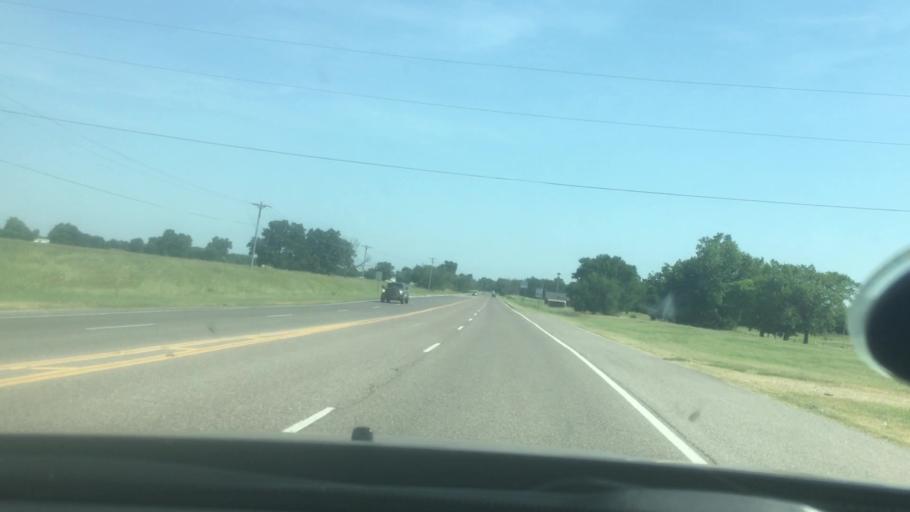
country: US
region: Oklahoma
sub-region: Murray County
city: Davis
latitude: 34.4639
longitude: -97.1305
